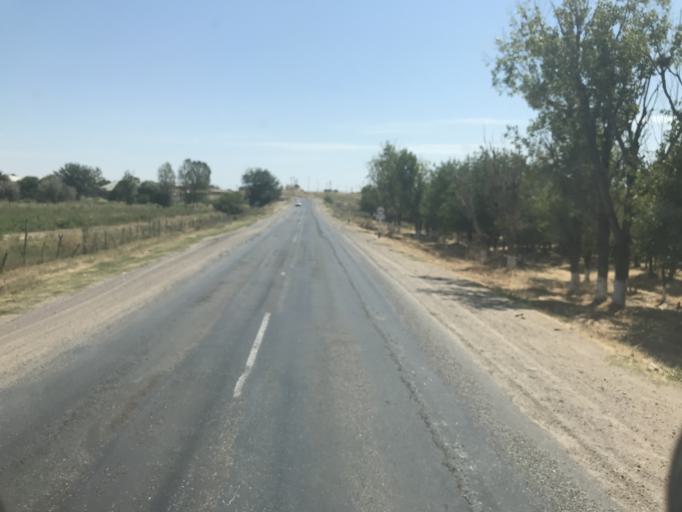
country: UZ
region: Toshkent
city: Yangiyul
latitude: 41.3727
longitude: 68.8286
